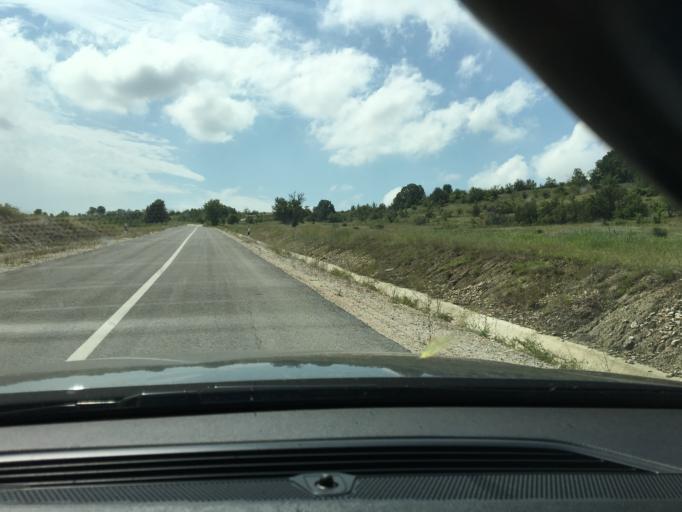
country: MK
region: Sveti Nikole
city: Gorobinci
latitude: 41.9154
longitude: 21.8791
